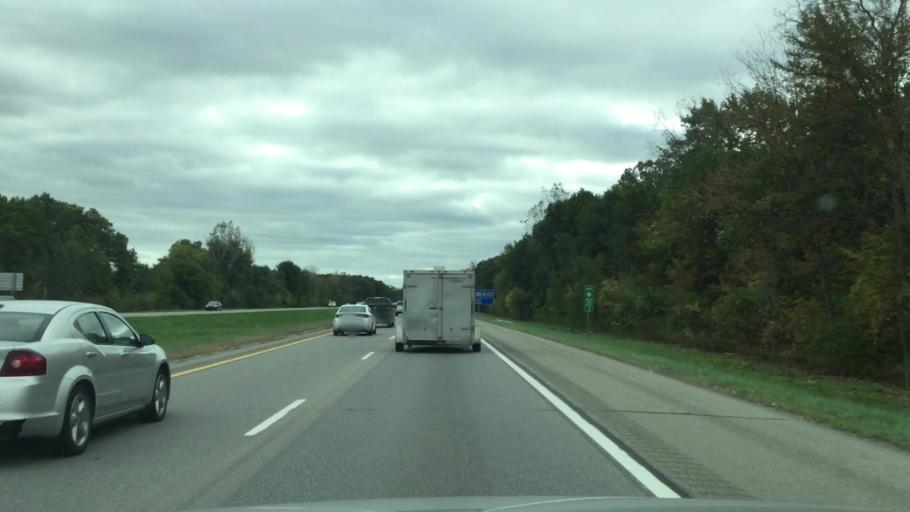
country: US
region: Michigan
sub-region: Macomb County
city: Shelby
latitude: 42.6926
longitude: -83.0216
